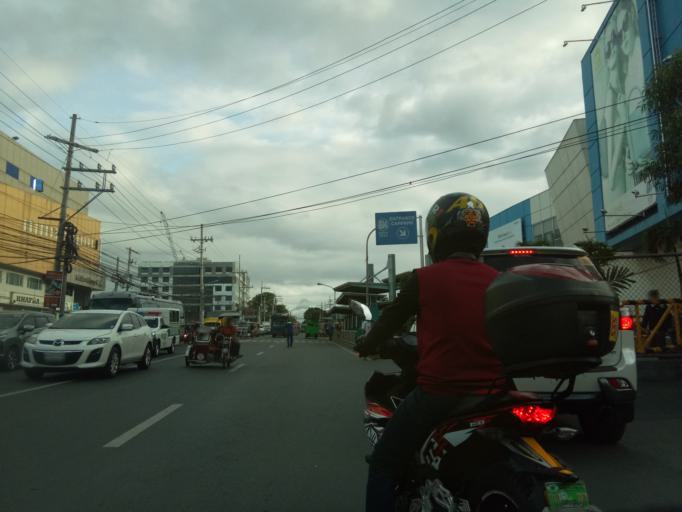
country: PH
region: Calabarzon
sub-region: Province of Cavite
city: Imus
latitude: 14.3849
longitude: 120.9780
